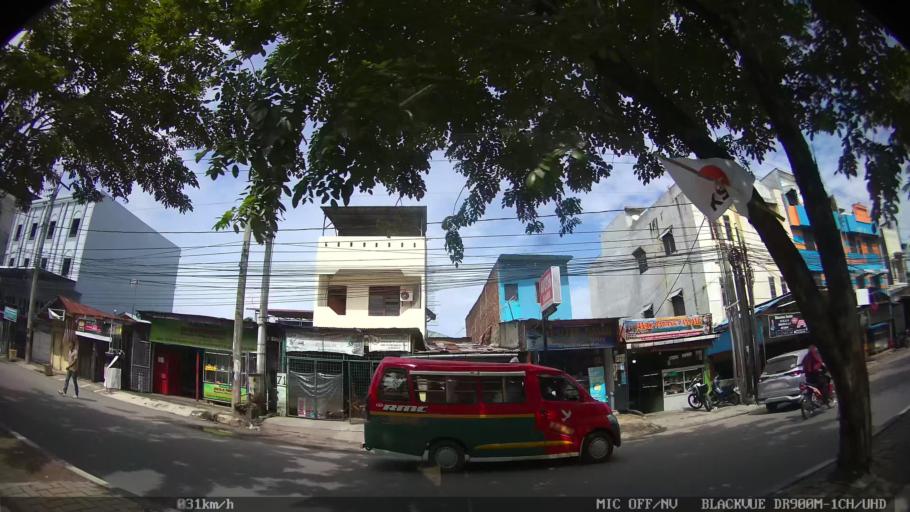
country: ID
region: North Sumatra
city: Medan
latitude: 3.6027
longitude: 98.7065
